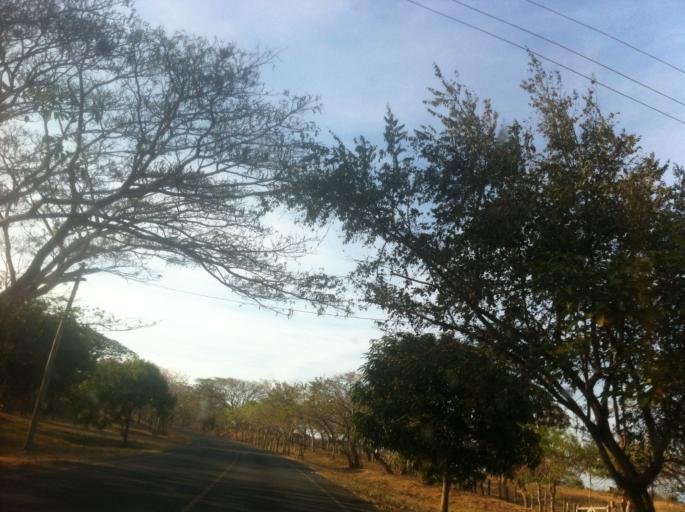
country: NI
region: Rivas
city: San Juan del Sur
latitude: 11.2960
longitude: -85.6865
